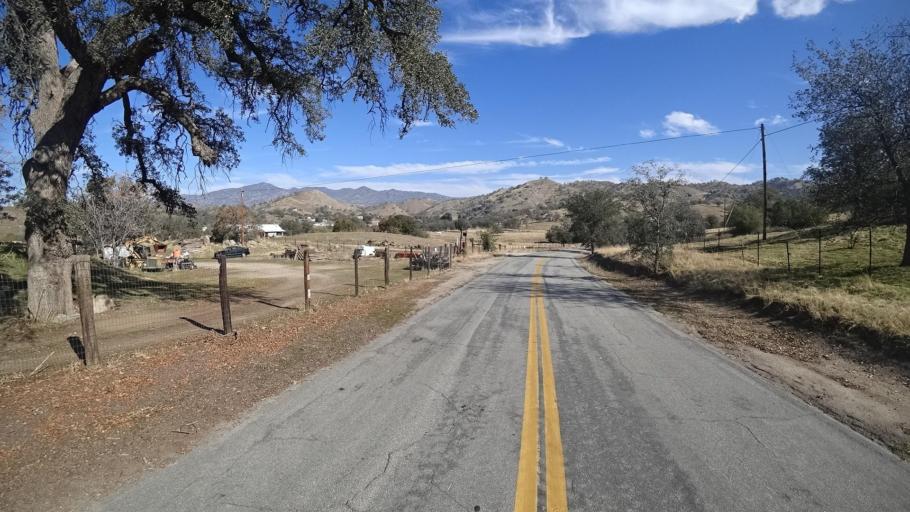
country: US
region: California
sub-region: Tulare County
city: Richgrove
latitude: 35.6997
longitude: -118.8425
